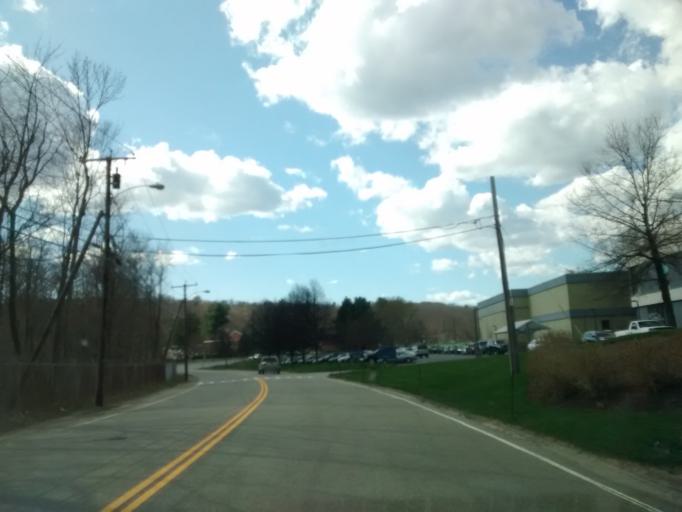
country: US
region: Massachusetts
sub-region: Worcester County
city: Worcester
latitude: 42.3043
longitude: -71.8153
